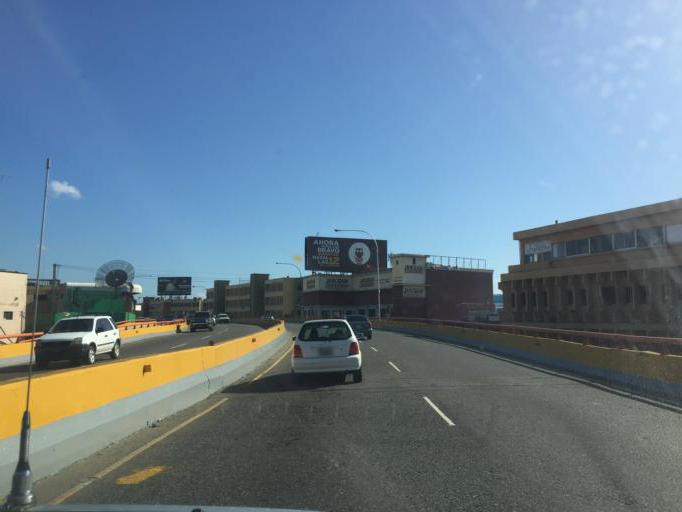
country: DO
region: Nacional
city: San Carlos
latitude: 18.4788
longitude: -69.8999
